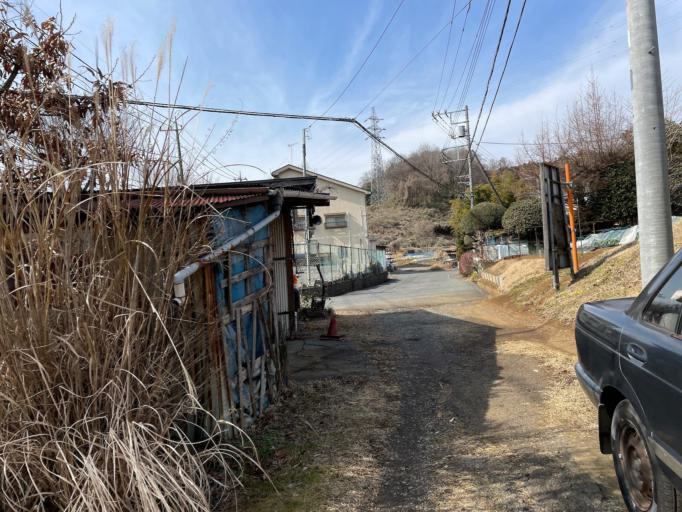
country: JP
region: Tokyo
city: Hino
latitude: 35.6319
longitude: 139.3714
